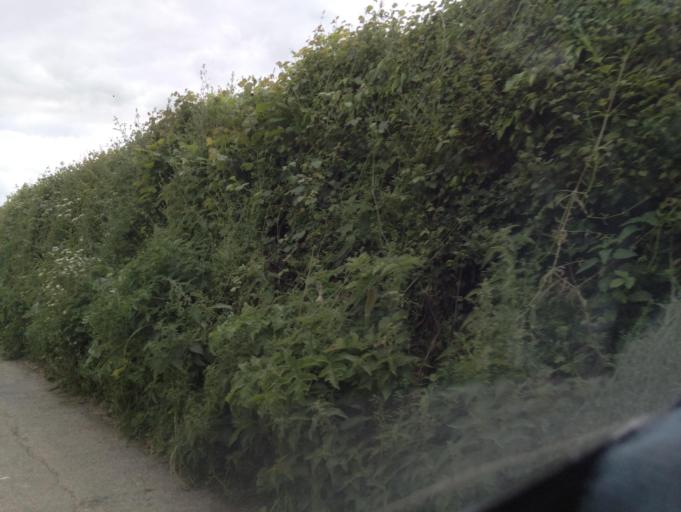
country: GB
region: England
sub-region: Herefordshire
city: Ledbury
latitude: 52.0340
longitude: -2.4572
